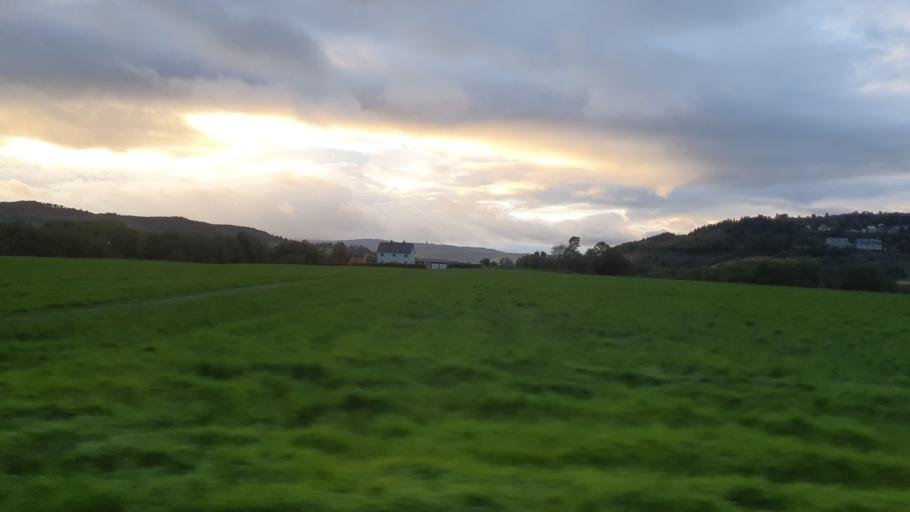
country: NO
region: Nord-Trondelag
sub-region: Levanger
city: Skogn
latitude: 63.6889
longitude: 11.1836
